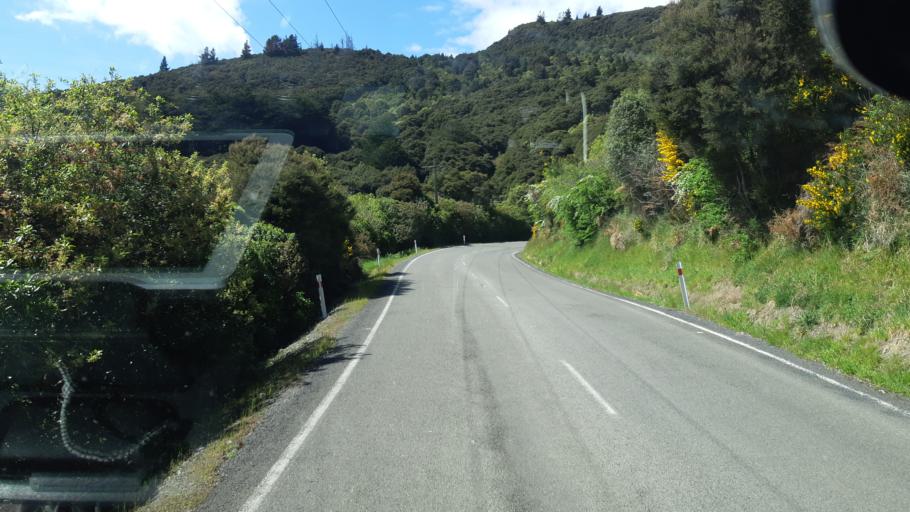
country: NZ
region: Otago
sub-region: Dunedin City
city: Portobello
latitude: -45.7797
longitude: 170.5971
